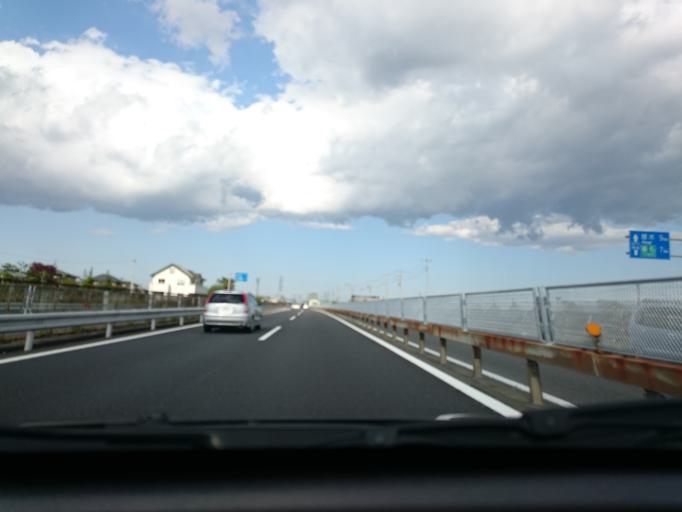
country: JP
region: Kanagawa
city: Isehara
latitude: 35.3744
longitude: 139.3208
